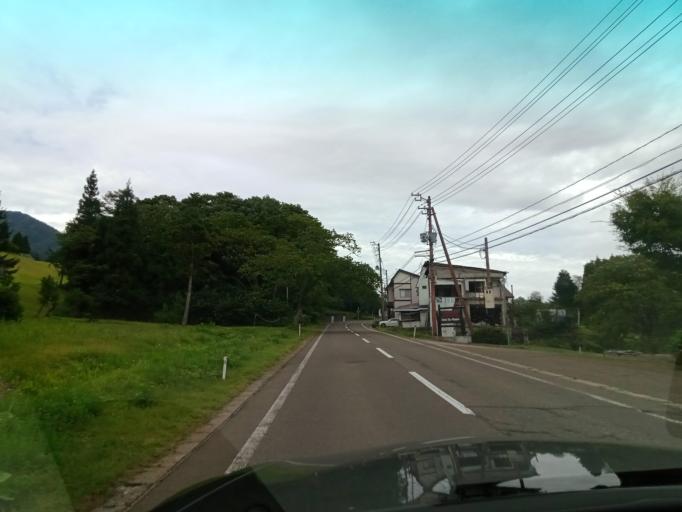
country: JP
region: Niigata
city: Arai
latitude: 36.8831
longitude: 138.1798
